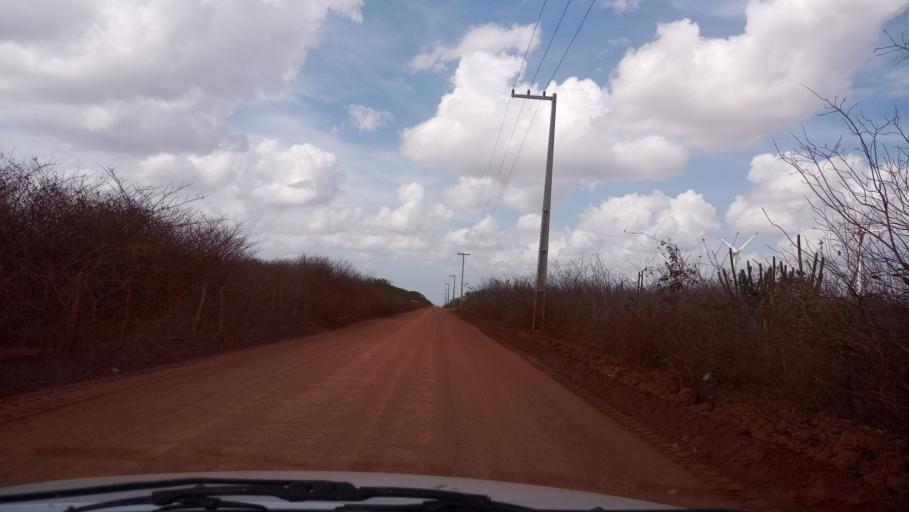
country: BR
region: Rio Grande do Norte
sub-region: Joao Camara
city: Joao Camara
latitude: -5.3596
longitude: -35.8339
